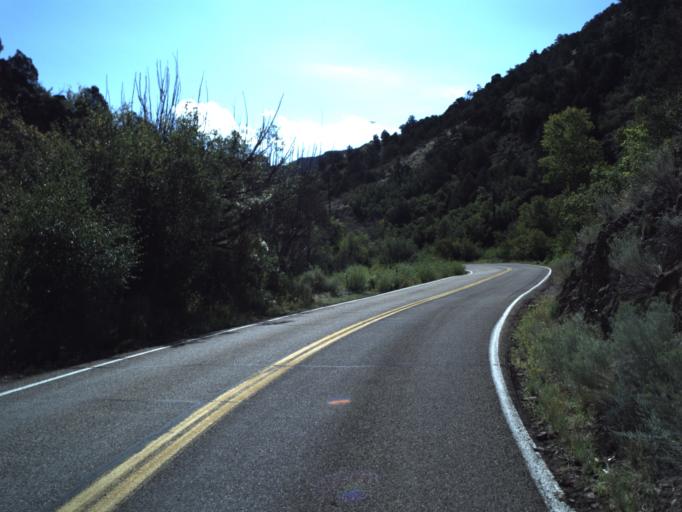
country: US
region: Utah
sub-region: Beaver County
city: Beaver
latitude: 38.2803
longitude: -112.5701
